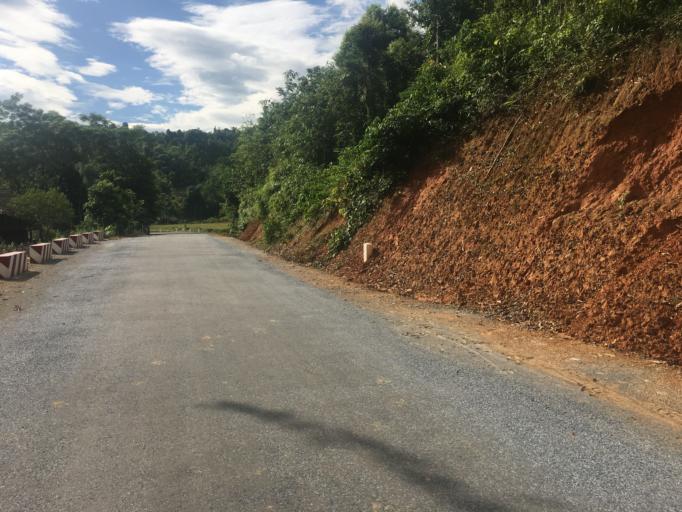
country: VN
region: Ha Giang
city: Thanh Pho Ha Giang
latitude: 22.8803
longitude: 105.0417
